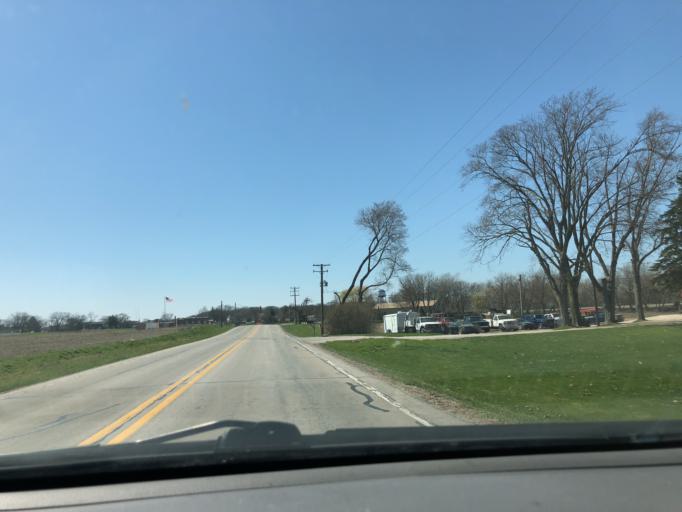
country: US
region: Illinois
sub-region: Kane County
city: Hampshire
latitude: 42.0481
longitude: -88.5408
